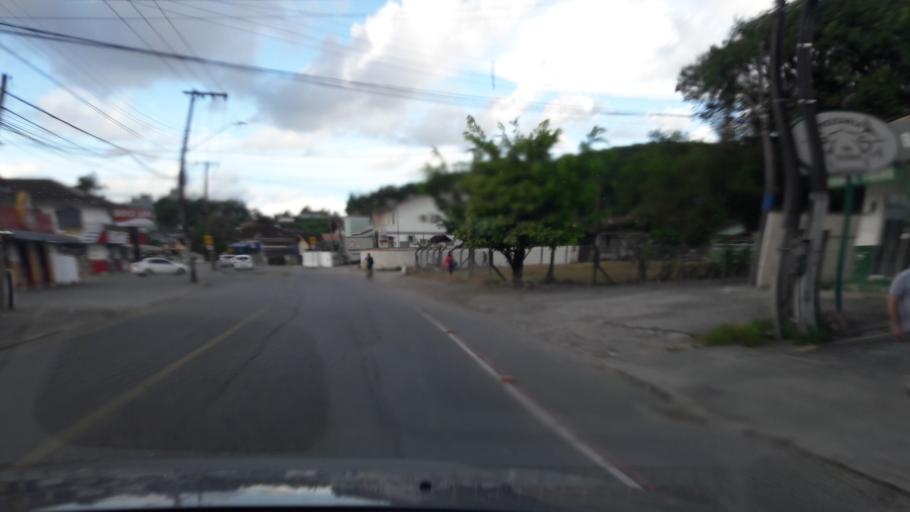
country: BR
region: Santa Catarina
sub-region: Joinville
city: Joinville
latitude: -26.3253
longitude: -48.8297
